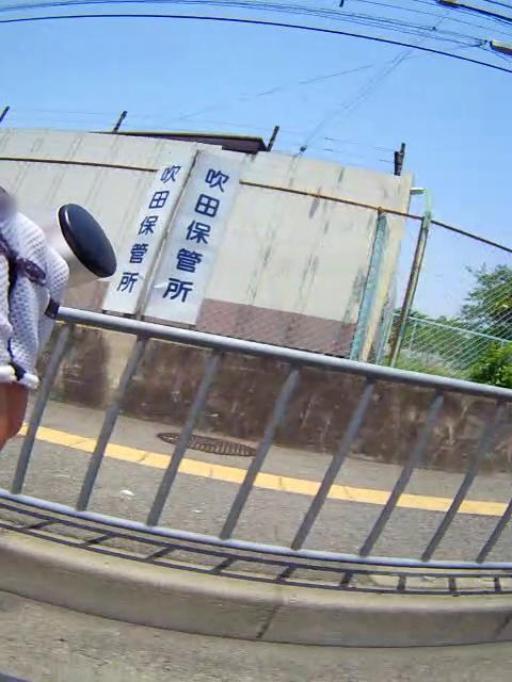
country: JP
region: Osaka
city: Suita
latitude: 34.7630
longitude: 135.5142
